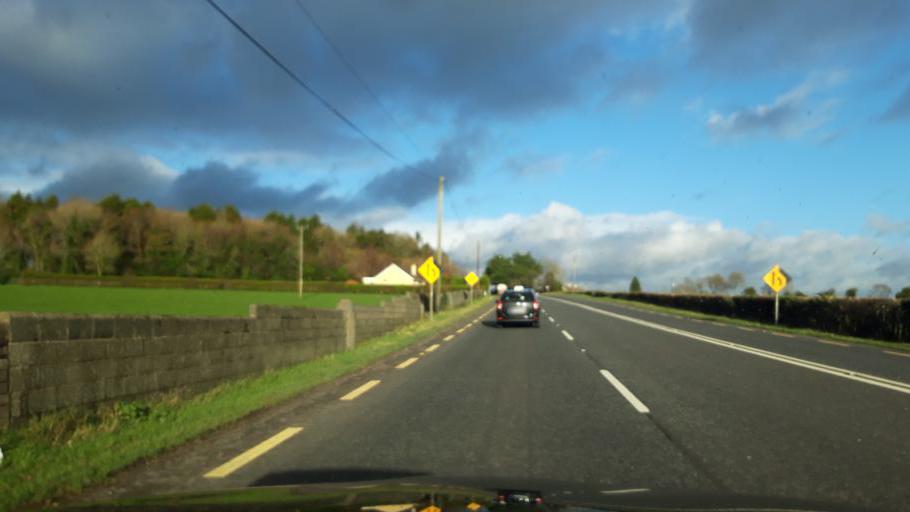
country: IE
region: Leinster
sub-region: An Mhi
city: Slane
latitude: 53.7202
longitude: -6.5261
